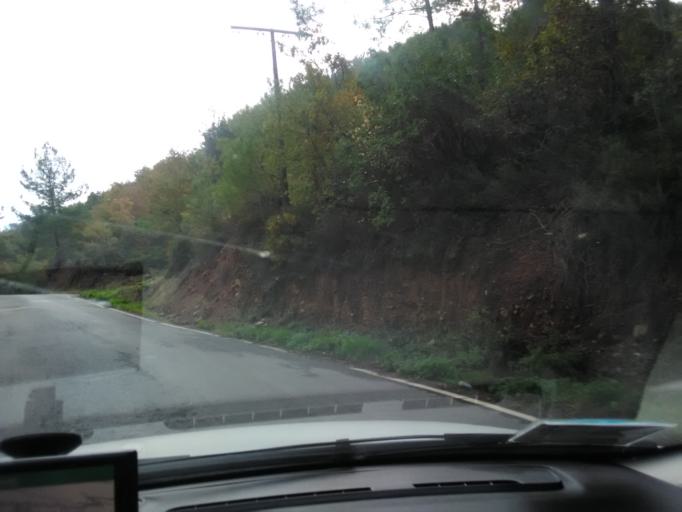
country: TR
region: Antalya
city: Gazipasa
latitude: 36.2551
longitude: 32.3931
